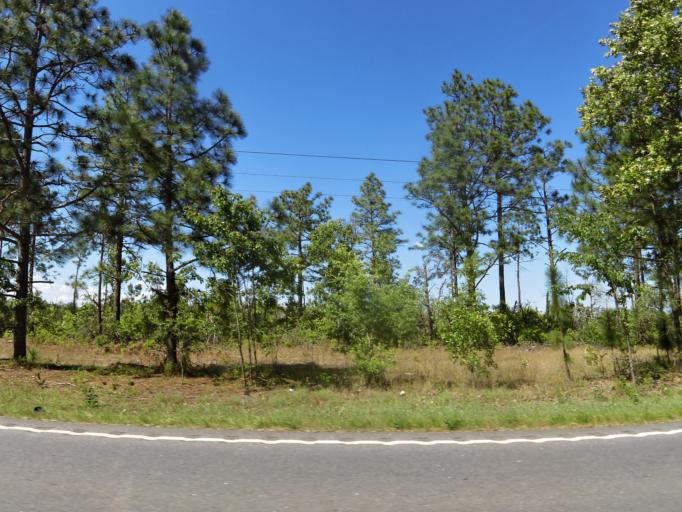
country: US
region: South Carolina
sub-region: Aiken County
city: New Ellenton
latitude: 33.5113
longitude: -81.5618
